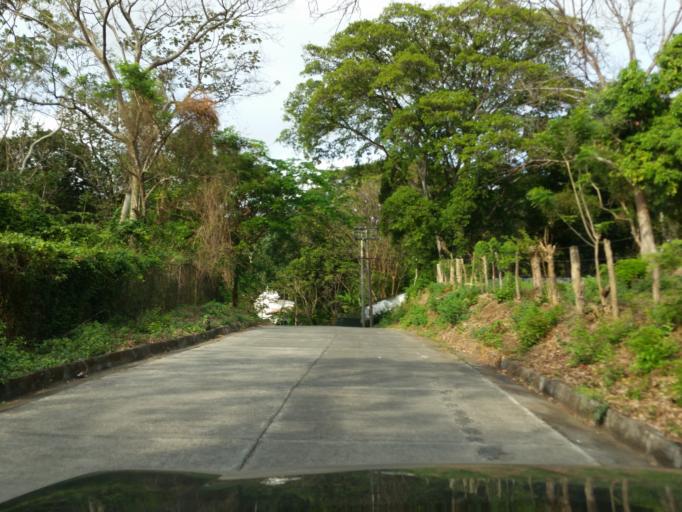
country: NI
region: Masaya
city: Ticuantepe
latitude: 12.0511
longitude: -86.2562
